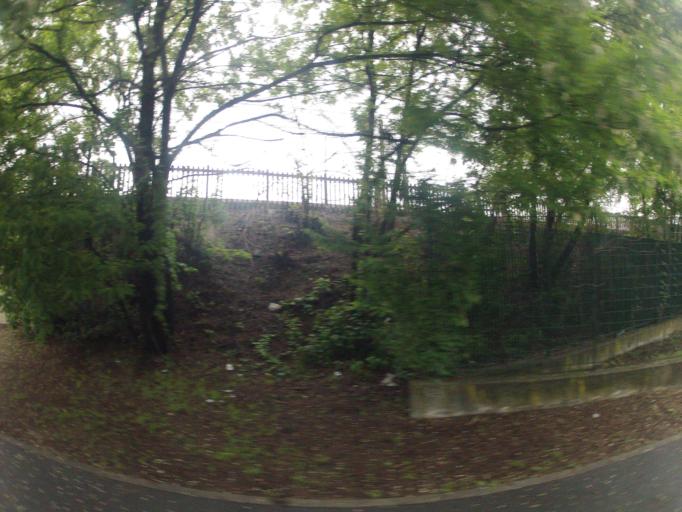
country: IT
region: Piedmont
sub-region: Provincia di Torino
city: Moncalieri
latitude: 45.0038
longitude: 7.6704
